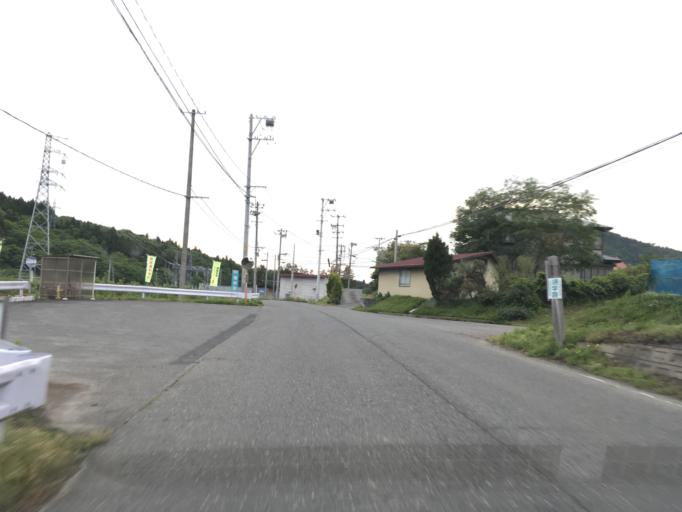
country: JP
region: Iwate
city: Mizusawa
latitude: 39.1746
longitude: 141.2963
